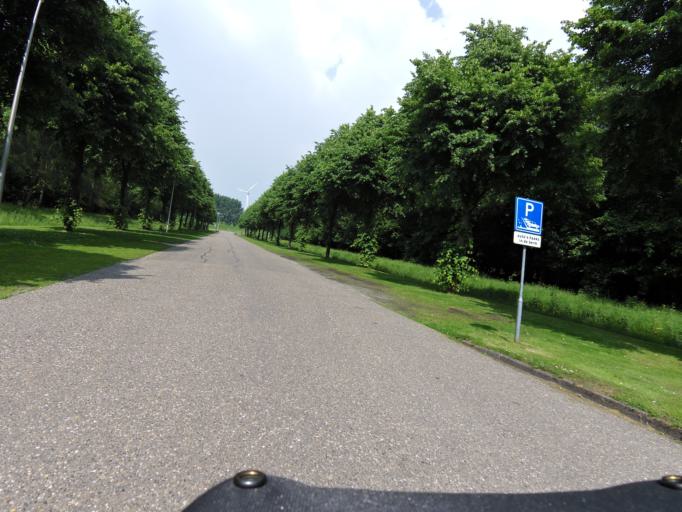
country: NL
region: South Holland
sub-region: Gemeente Spijkenisse
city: Spijkenisse
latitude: 51.8611
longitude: 4.3017
